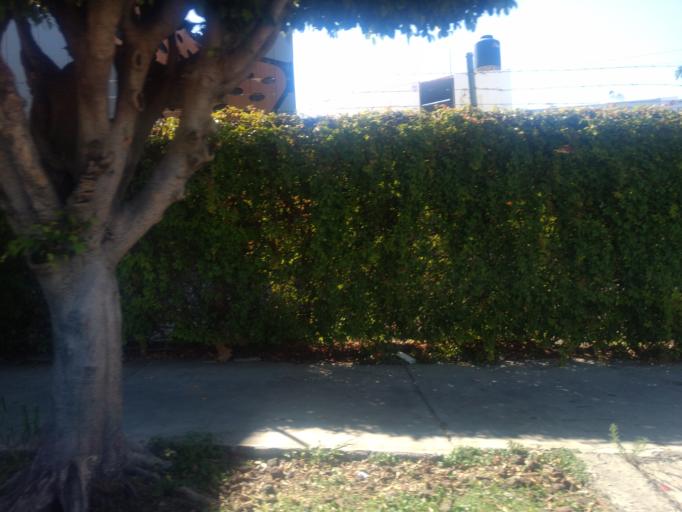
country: MX
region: Jalisco
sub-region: Zapopan
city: Zapopan
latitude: 20.6995
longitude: -103.3759
